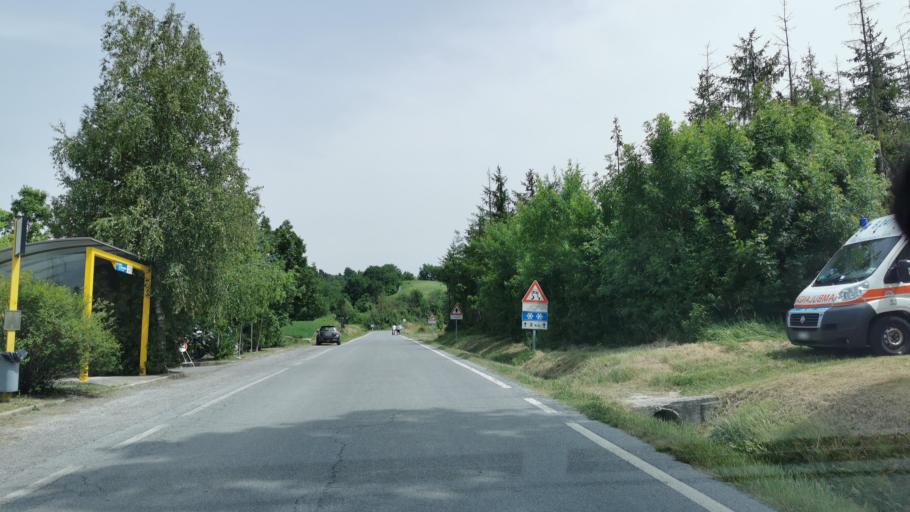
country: IT
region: Piedmont
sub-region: Provincia di Cuneo
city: Sale San Giovanni
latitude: 44.4043
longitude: 8.0753
